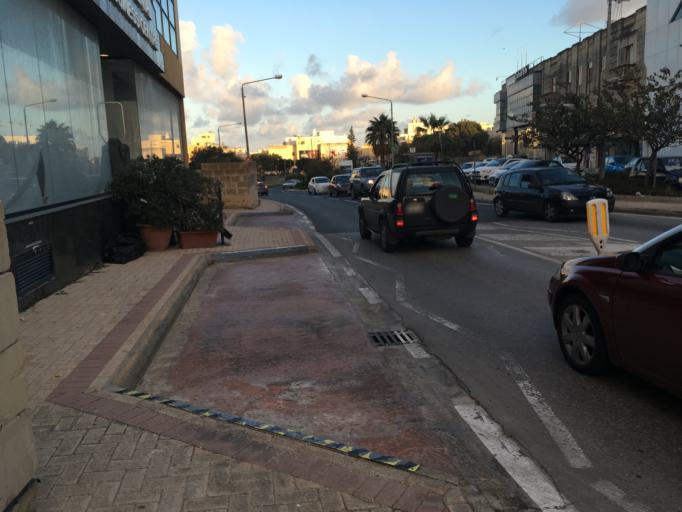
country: MT
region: L-Imsida
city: Imsida
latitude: 35.8925
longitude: 14.4815
